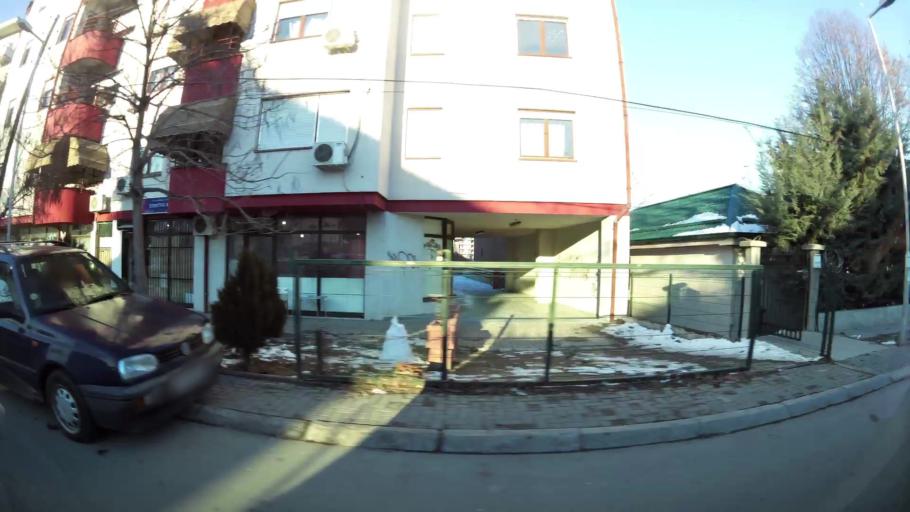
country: MK
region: Karpos
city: Skopje
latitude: 41.9965
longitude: 21.3945
